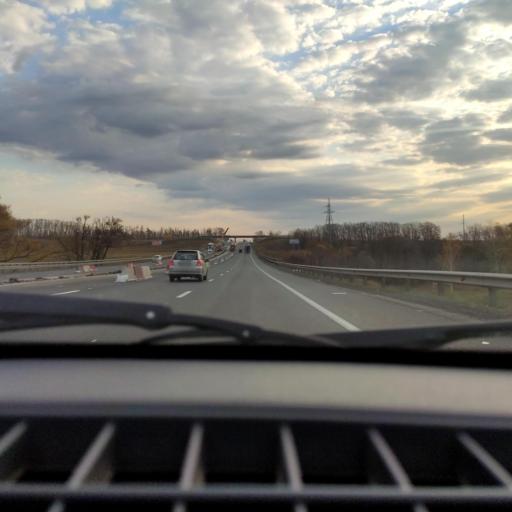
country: RU
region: Bashkortostan
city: Avdon
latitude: 54.6666
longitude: 55.7472
